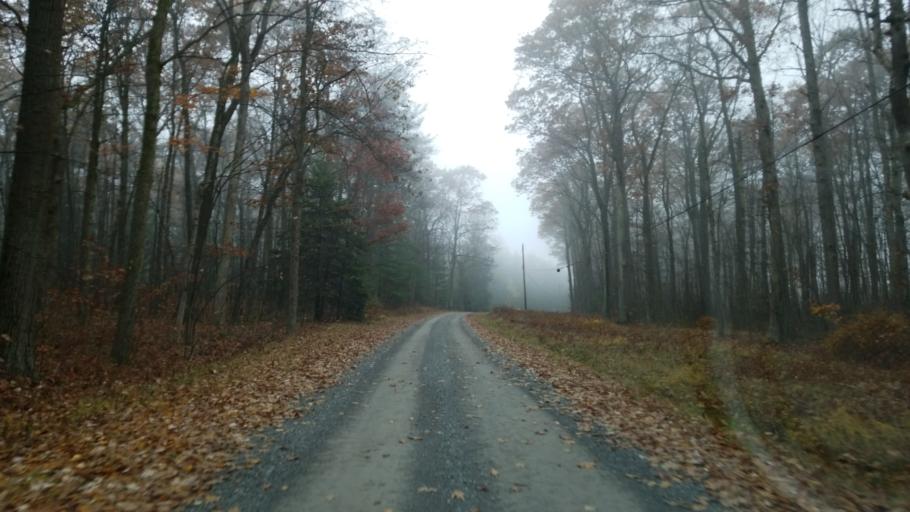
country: US
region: Pennsylvania
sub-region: Clearfield County
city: Clearfield
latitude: 41.1007
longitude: -78.5263
